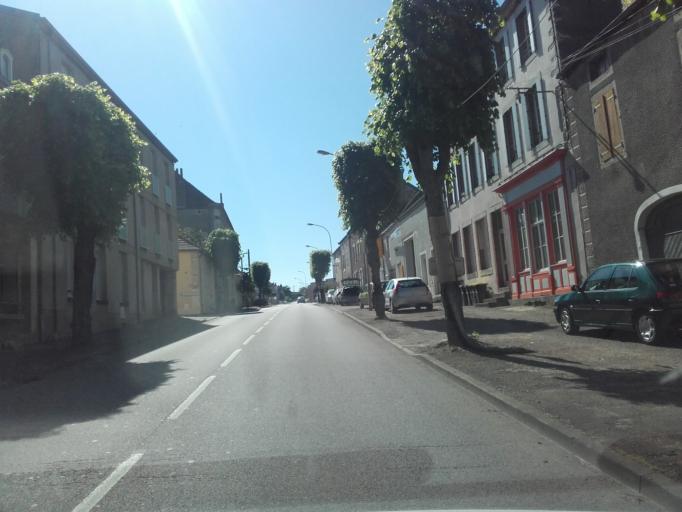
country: FR
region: Bourgogne
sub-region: Departement de la Cote-d'Or
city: Nolay
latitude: 46.9507
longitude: 4.6366
